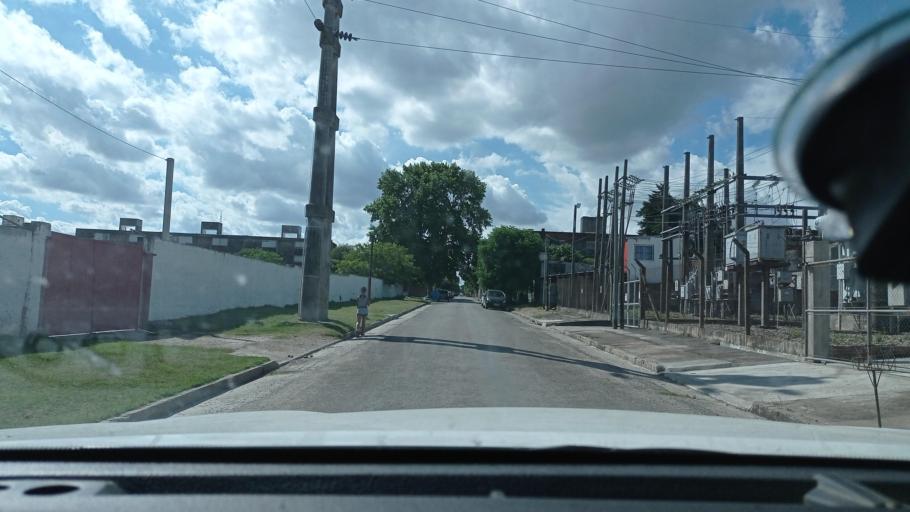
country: UY
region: Florida
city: Florida
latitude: -34.1040
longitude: -56.2070
